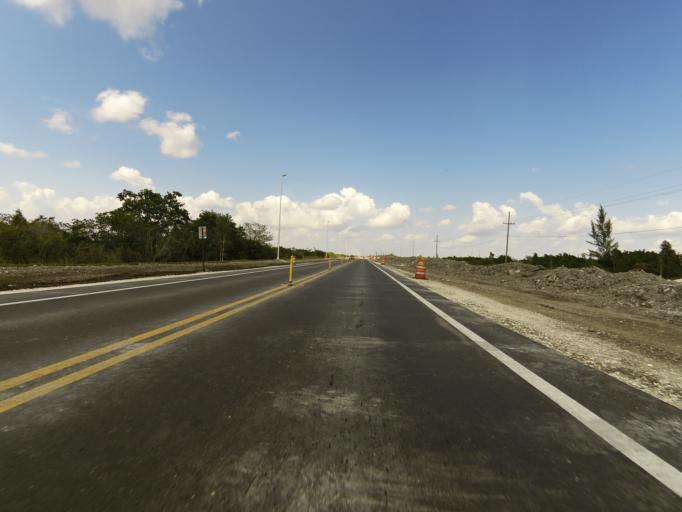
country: US
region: Florida
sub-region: Miami-Dade County
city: Doral
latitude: 25.9001
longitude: -80.4773
